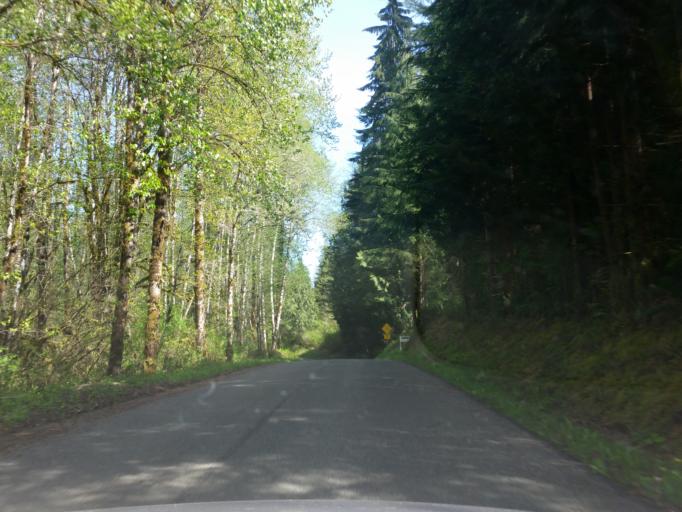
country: US
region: Washington
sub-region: Snohomish County
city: Woods Creek
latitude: 47.9725
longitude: -121.8694
